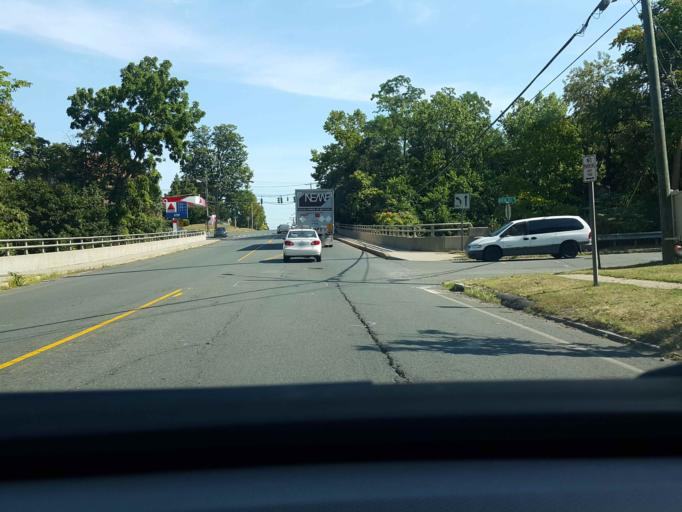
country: US
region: Connecticut
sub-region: Middlesex County
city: Middletown
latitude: 41.5488
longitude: -72.6504
